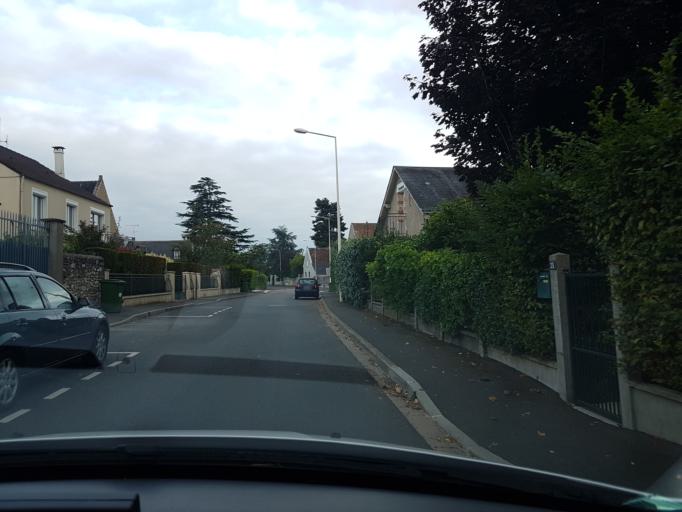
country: FR
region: Centre
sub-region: Departement d'Indre-et-Loire
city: Saint-Avertin
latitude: 47.3651
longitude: 0.7385
